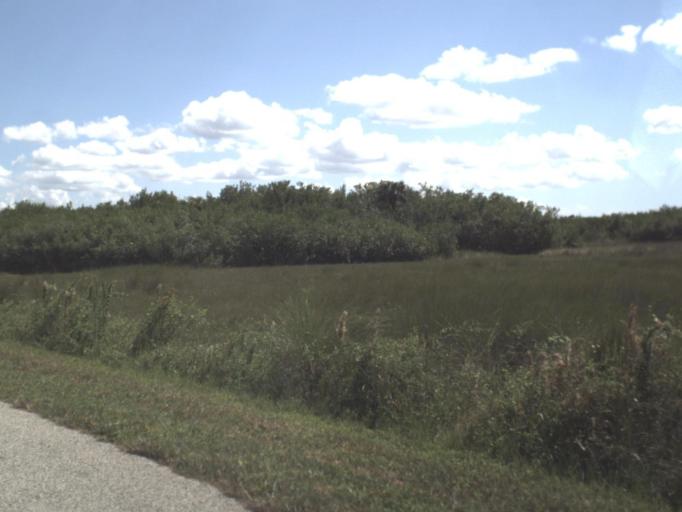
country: US
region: Florida
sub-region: Collier County
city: Marco
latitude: 25.9359
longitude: -81.4550
